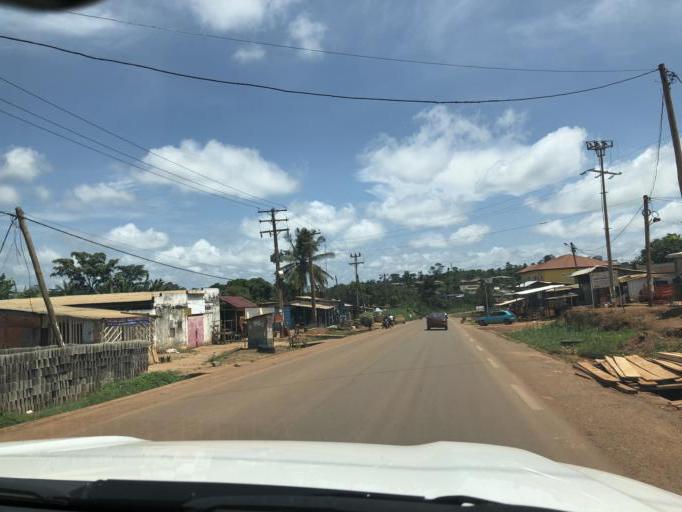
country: CM
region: Centre
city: Yaounde
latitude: 3.8644
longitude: 11.6146
